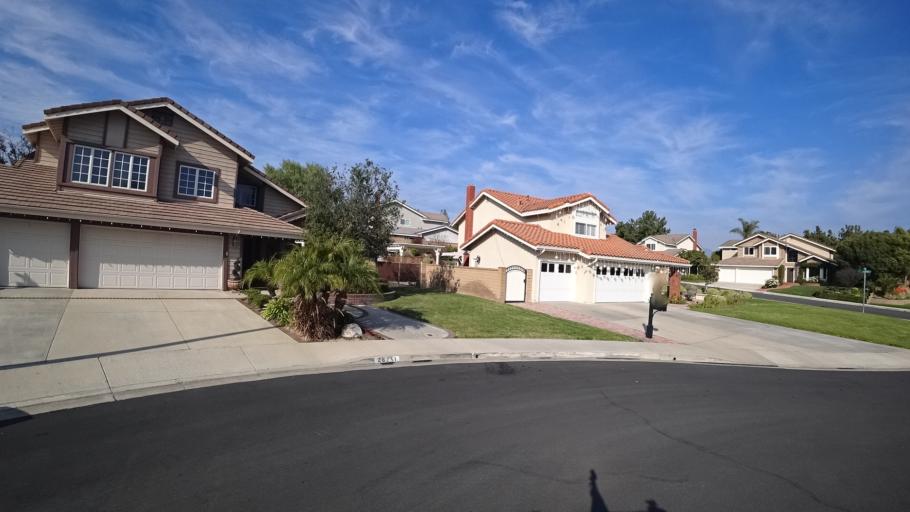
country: US
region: California
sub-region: Orange County
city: Lake Forest
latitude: 33.6460
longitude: -117.6729
